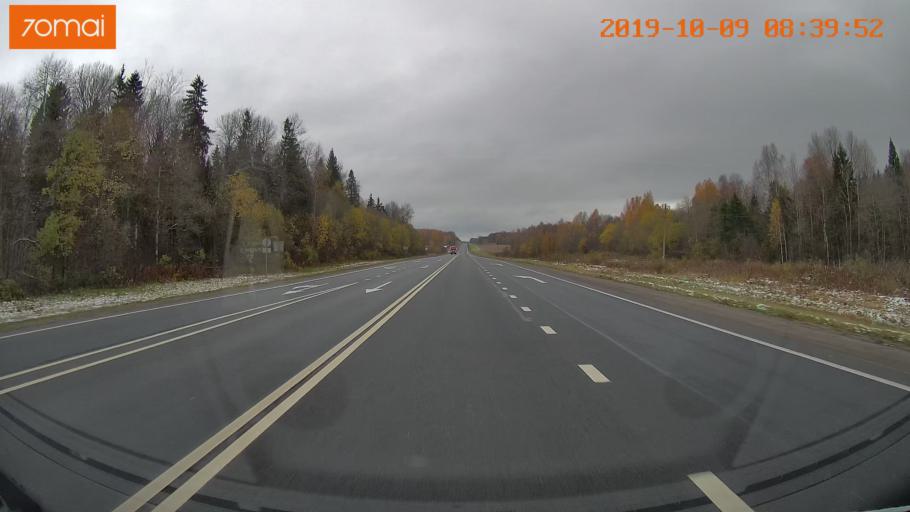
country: RU
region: Vologda
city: Gryazovets
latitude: 58.9779
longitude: 40.1477
